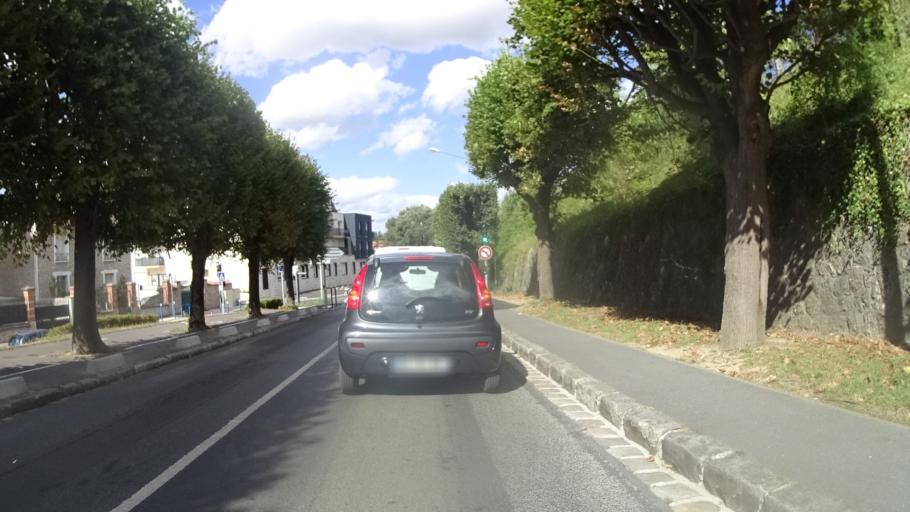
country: FR
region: Ile-de-France
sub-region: Departement de l'Essonne
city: La Ferte-Alais
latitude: 48.4865
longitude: 2.3519
